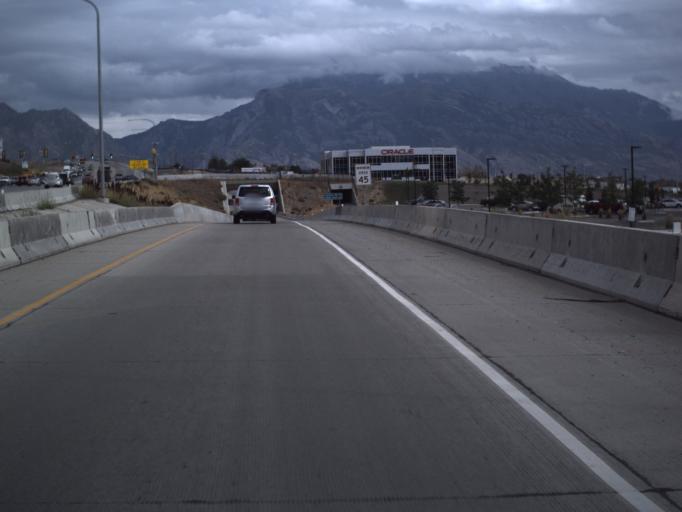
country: US
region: Utah
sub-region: Utah County
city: Lehi
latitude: 40.4314
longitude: -111.8843
